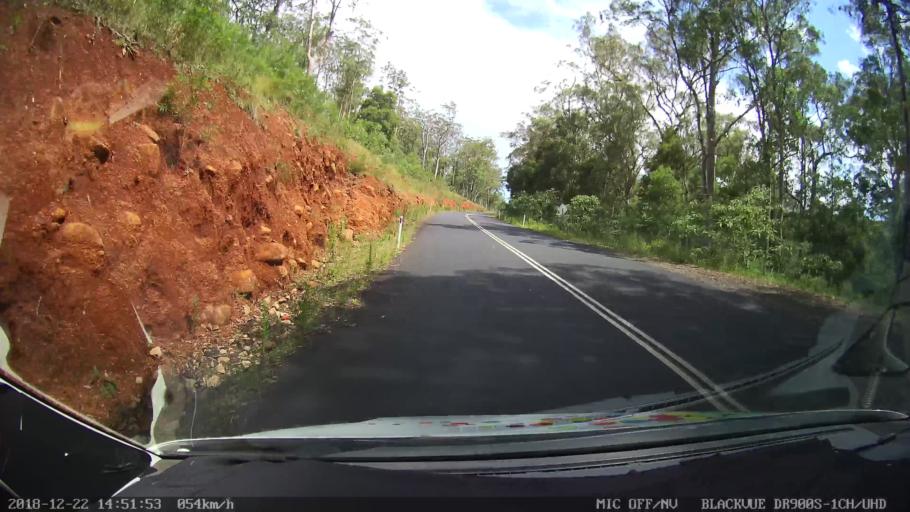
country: AU
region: New South Wales
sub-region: Bellingen
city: Dorrigo
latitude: -30.2055
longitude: 152.5436
